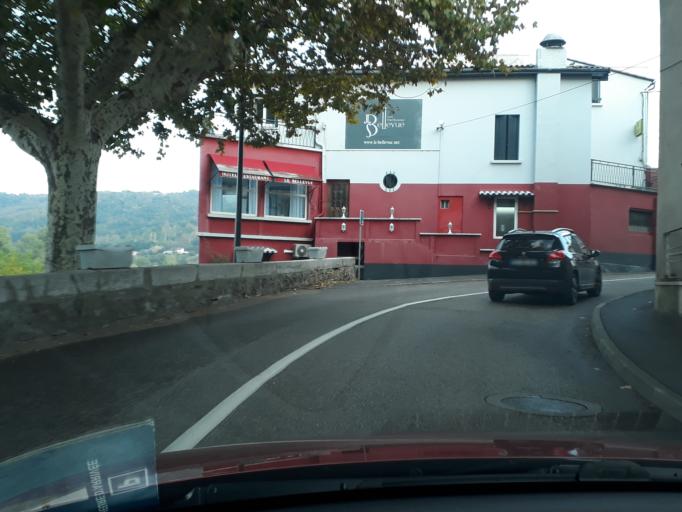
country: FR
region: Rhone-Alpes
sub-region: Departement de l'Isere
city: Les Roches-de-Condrieu
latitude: 45.4557
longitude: 4.7700
